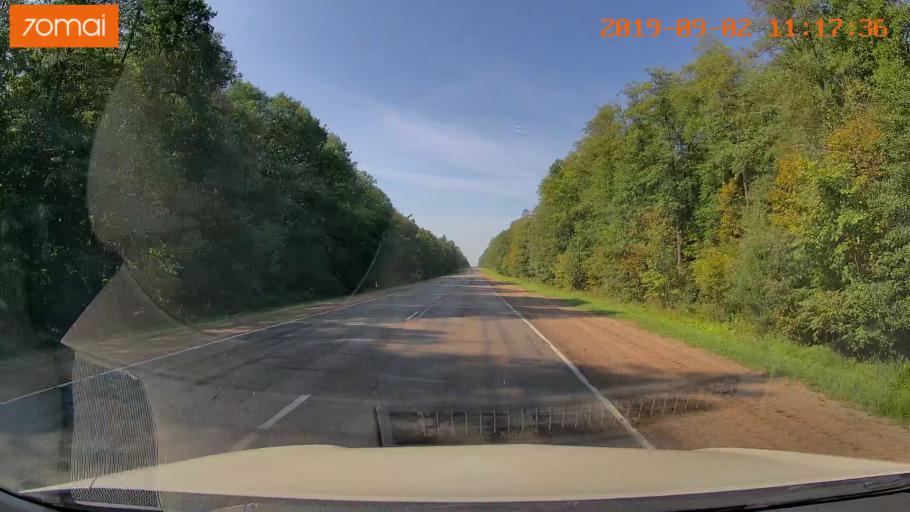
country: RU
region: Smolensk
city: Yekimovichi
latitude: 54.0606
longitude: 33.1149
